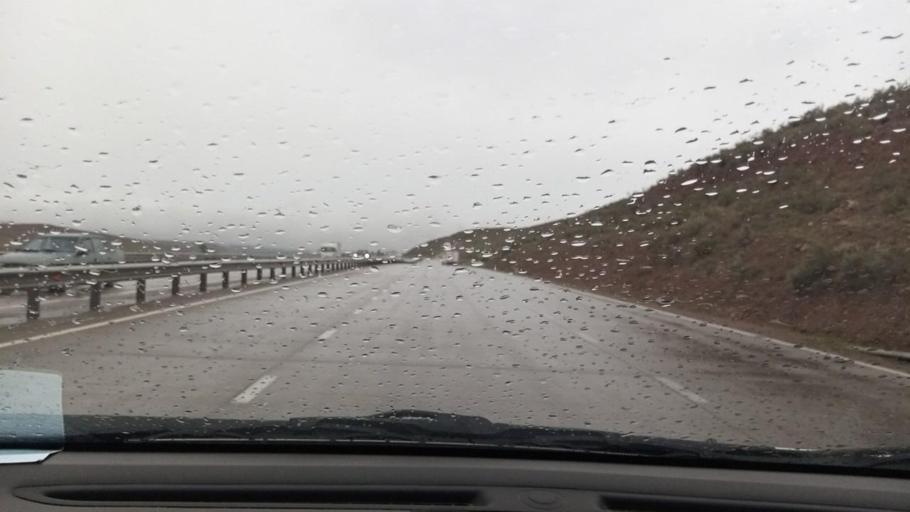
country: UZ
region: Namangan
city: Pop Shahri
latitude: 40.9280
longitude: 70.7154
